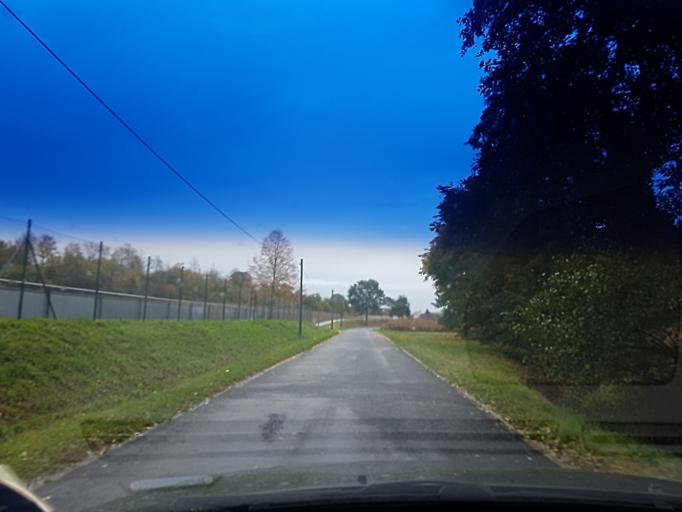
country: DE
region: Bavaria
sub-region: Regierungsbezirk Mittelfranken
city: Wachenroth
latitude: 49.7542
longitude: 10.7019
